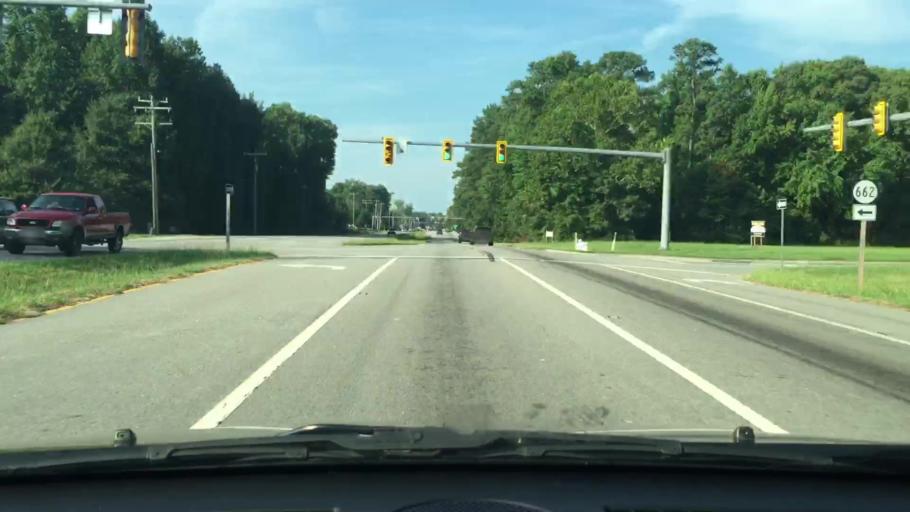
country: US
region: Virginia
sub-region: Isle of Wight County
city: Carrollton
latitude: 36.9576
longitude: -76.5246
